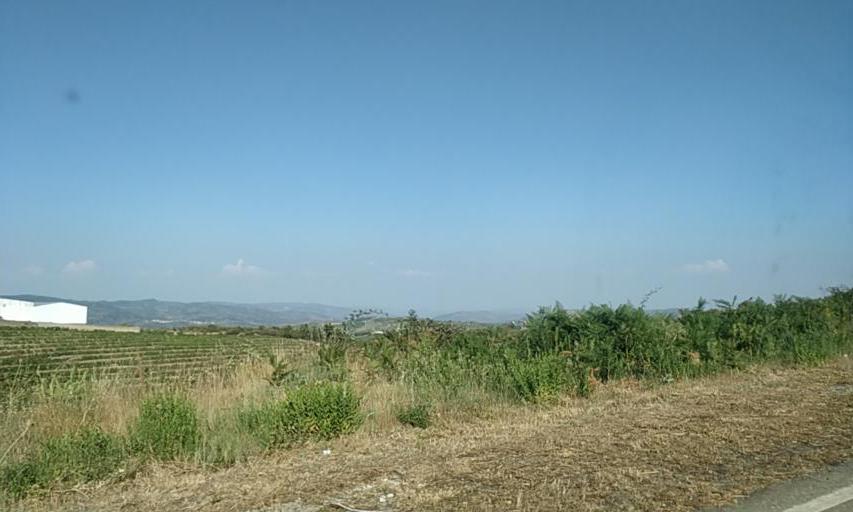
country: PT
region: Viseu
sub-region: Sao Joao da Pesqueira
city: Sao Joao da Pesqueira
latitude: 41.1599
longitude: -7.4368
